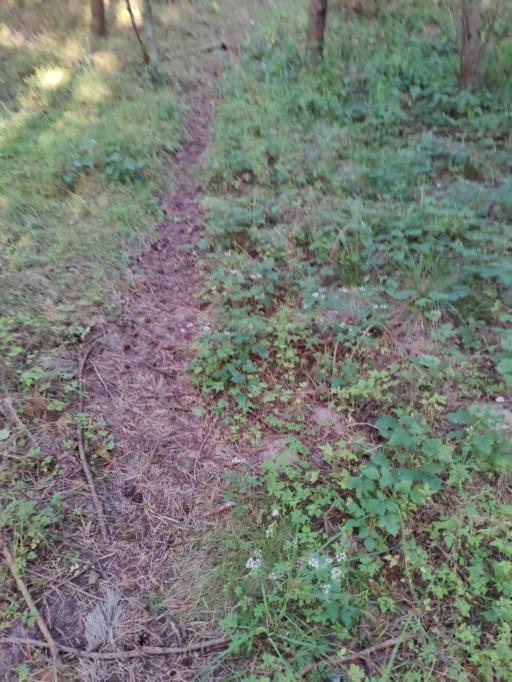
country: DK
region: South Denmark
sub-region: Middelfart Kommune
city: Ejby
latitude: 55.3798
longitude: 9.9352
